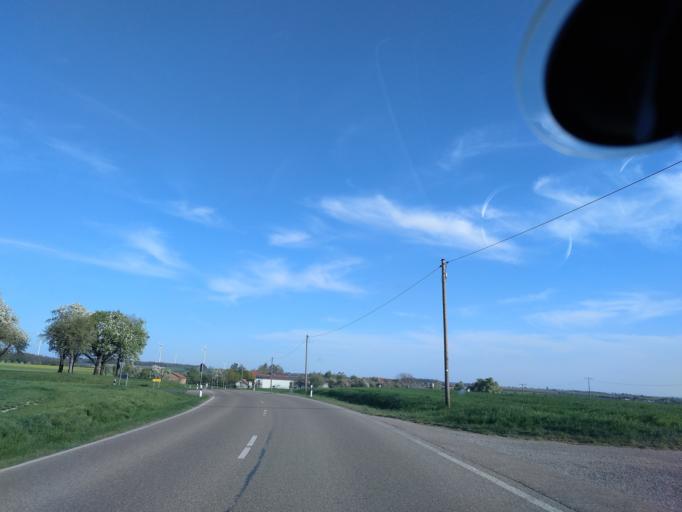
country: DE
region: Baden-Wuerttemberg
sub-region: Regierungsbezirk Stuttgart
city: Langenburg
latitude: 49.2197
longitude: 9.8501
